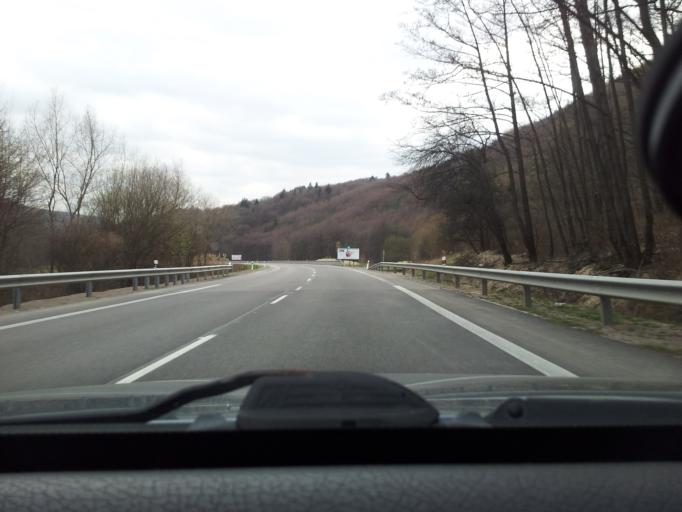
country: SK
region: Banskobystricky
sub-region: Okres Ziar nad Hronom
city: Kremnica
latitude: 48.6406
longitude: 18.9021
